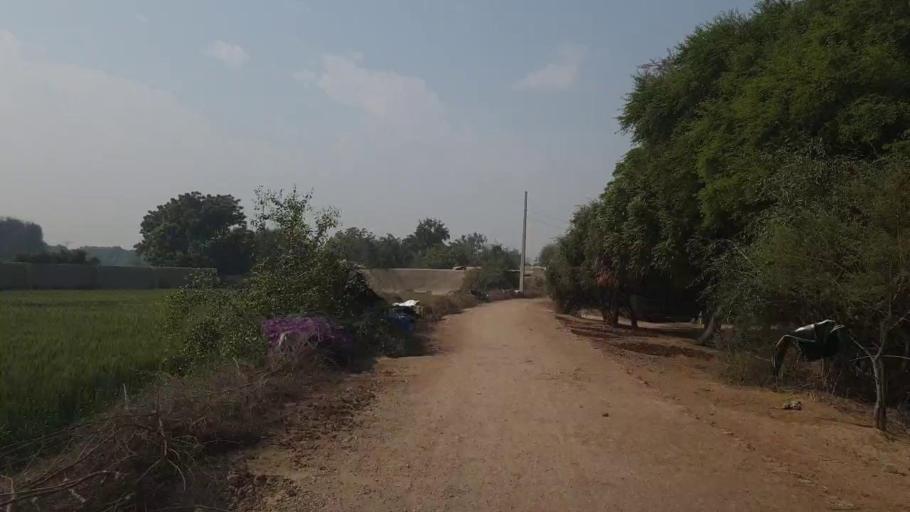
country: PK
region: Sindh
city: Hala
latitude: 25.7941
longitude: 68.4427
